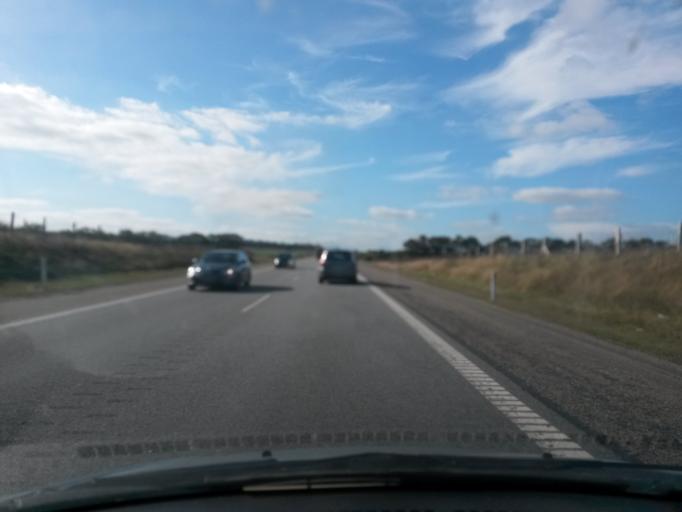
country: DK
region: Central Jutland
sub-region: Herning Kommune
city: Snejbjerg
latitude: 56.1878
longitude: 8.9303
